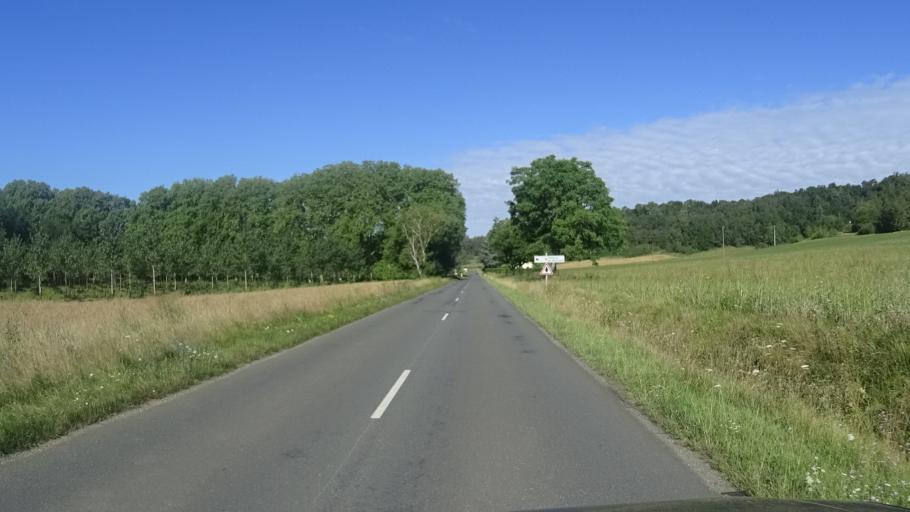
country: FR
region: Aquitaine
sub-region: Departement de la Dordogne
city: Sourzac
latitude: 45.0161
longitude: 0.4414
